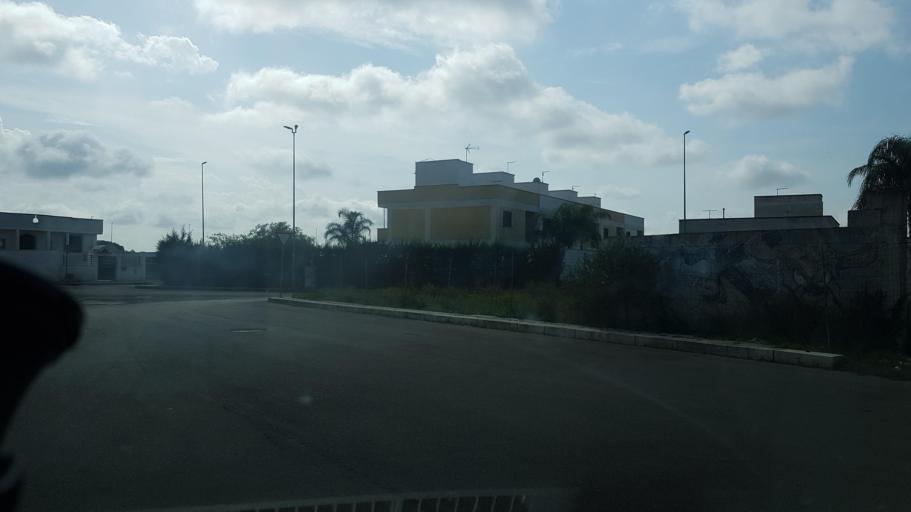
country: IT
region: Apulia
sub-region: Provincia di Brindisi
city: San Donaci
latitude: 40.4484
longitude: 17.9304
